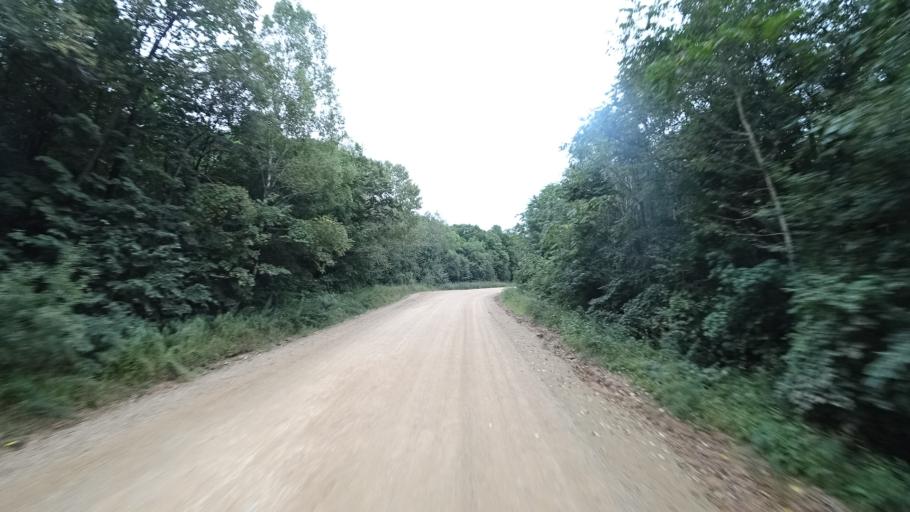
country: RU
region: Primorskiy
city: Rettikhovka
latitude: 44.1848
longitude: 132.8182
